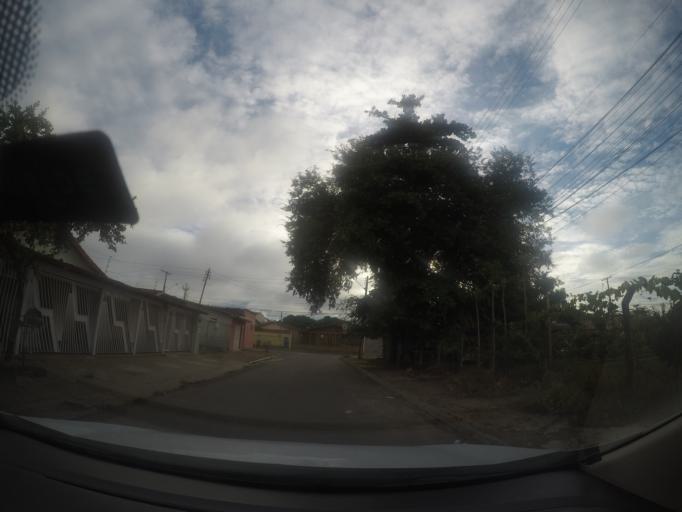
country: BR
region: Goias
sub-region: Goiania
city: Goiania
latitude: -16.6838
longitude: -49.3120
